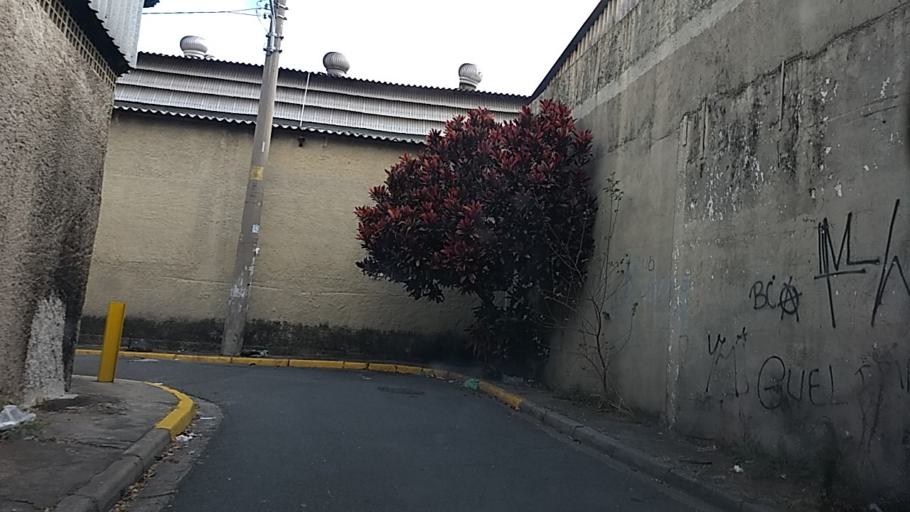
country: BR
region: Sao Paulo
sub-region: Sao Paulo
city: Sao Paulo
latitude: -23.5166
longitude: -46.5958
